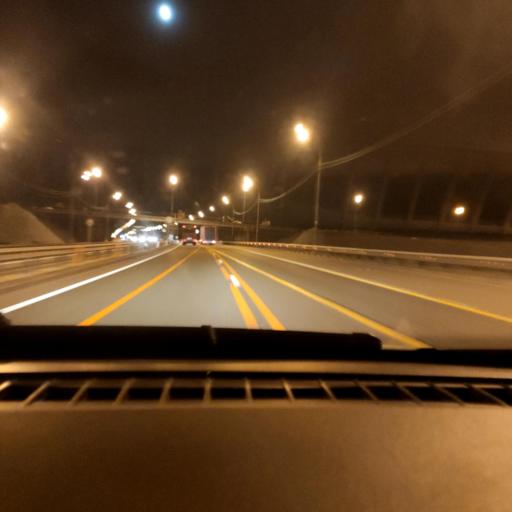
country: RU
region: Lipetsk
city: Khlevnoye
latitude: 52.2393
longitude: 39.0713
